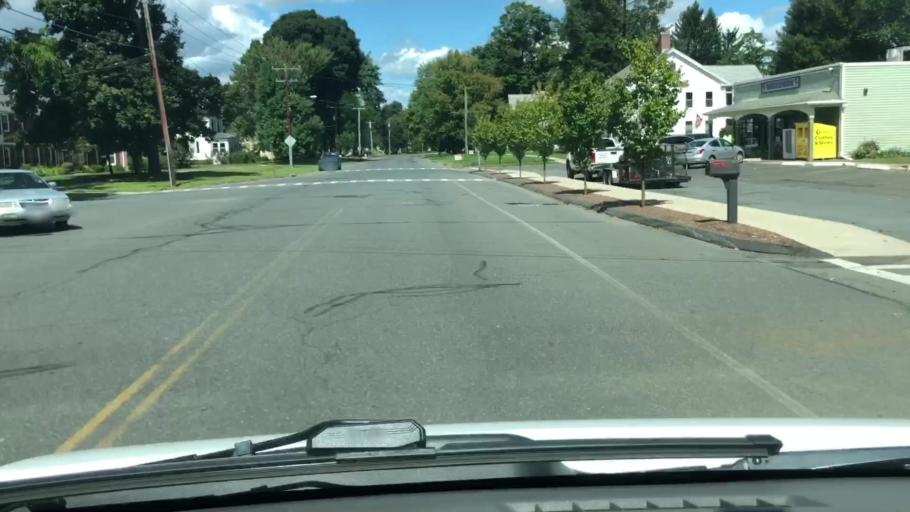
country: US
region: Massachusetts
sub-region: Hampshire County
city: Hatfield
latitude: 42.3730
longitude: -72.5962
